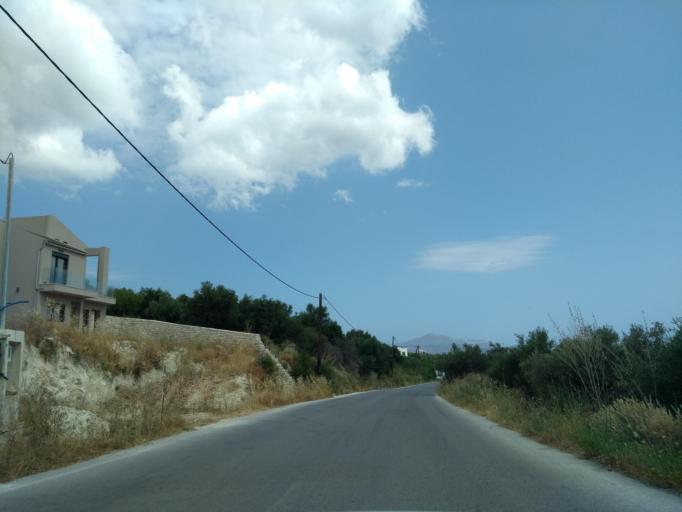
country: GR
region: Crete
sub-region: Nomos Chanias
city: Kalivai
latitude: 35.4395
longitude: 24.1754
